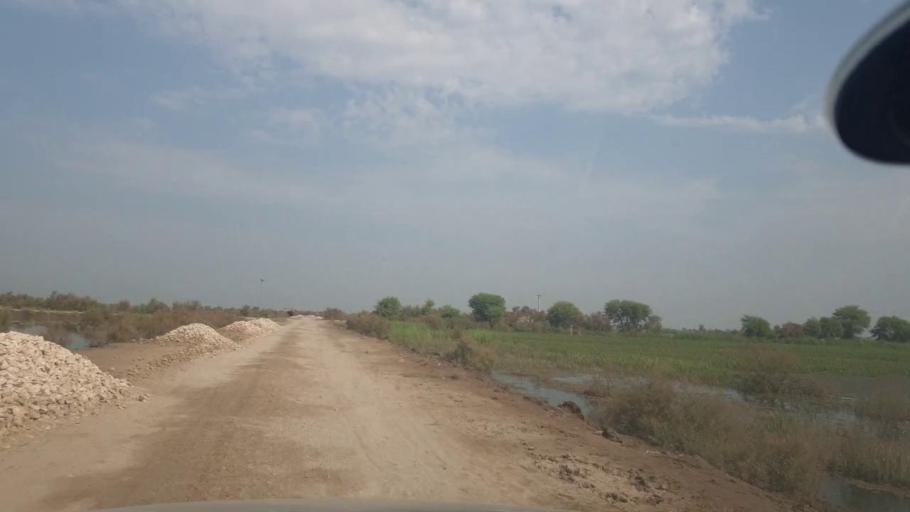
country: PK
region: Balochistan
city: Mehrabpur
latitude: 28.0884
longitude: 68.0972
